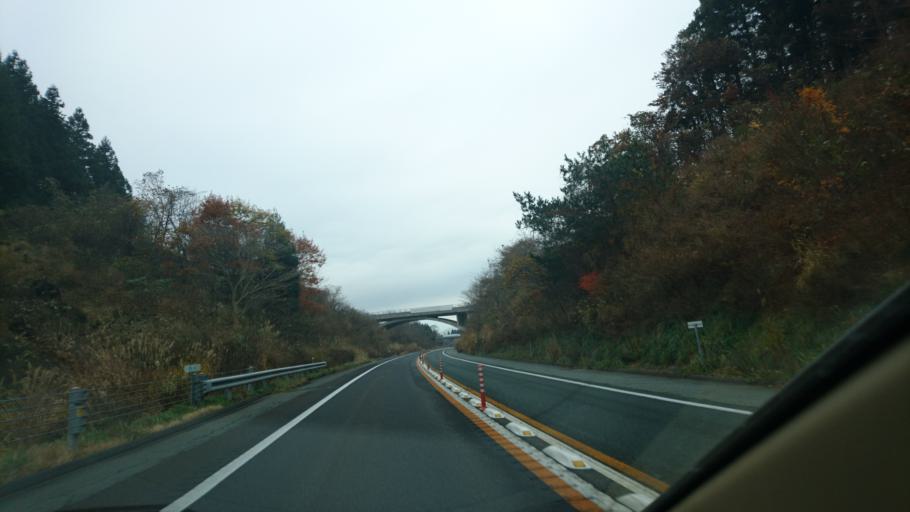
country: JP
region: Iwate
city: Kitakami
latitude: 39.2798
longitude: 141.0173
